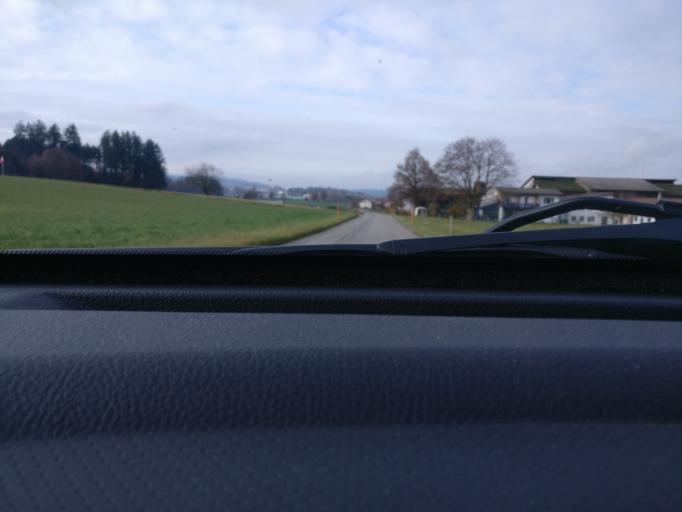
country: CH
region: Bern
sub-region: Bern-Mittelland District
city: Urtenen
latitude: 47.0075
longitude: 7.4896
